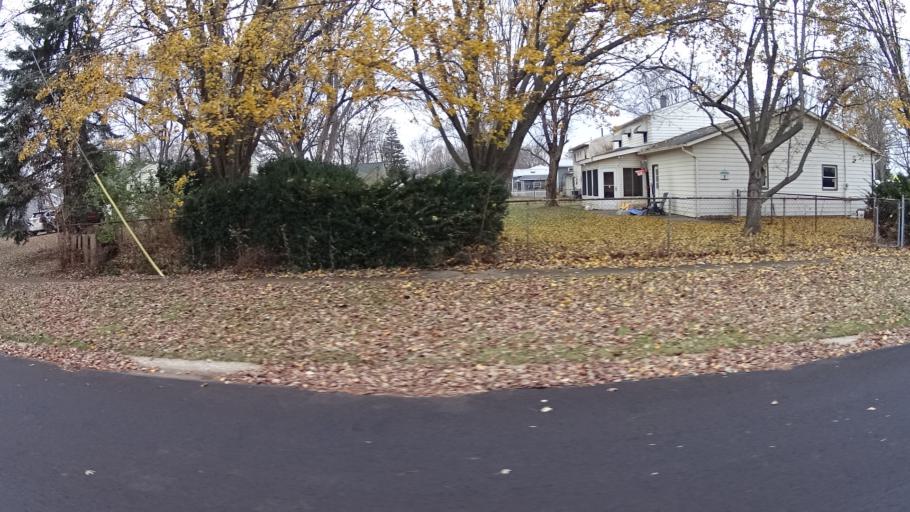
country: US
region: Ohio
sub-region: Lorain County
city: North Ridgeville
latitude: 41.3847
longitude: -81.9991
